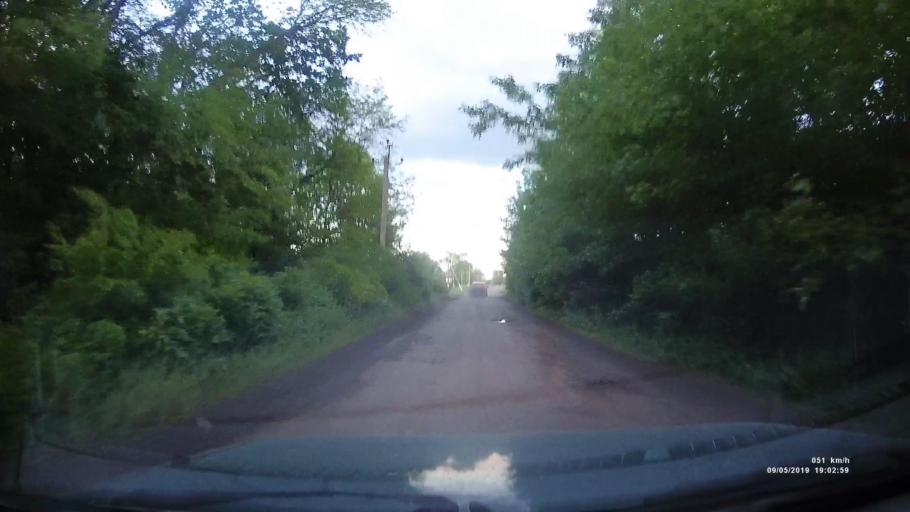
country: RU
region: Krasnodarskiy
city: Kanelovskaya
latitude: 46.7437
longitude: 39.1588
